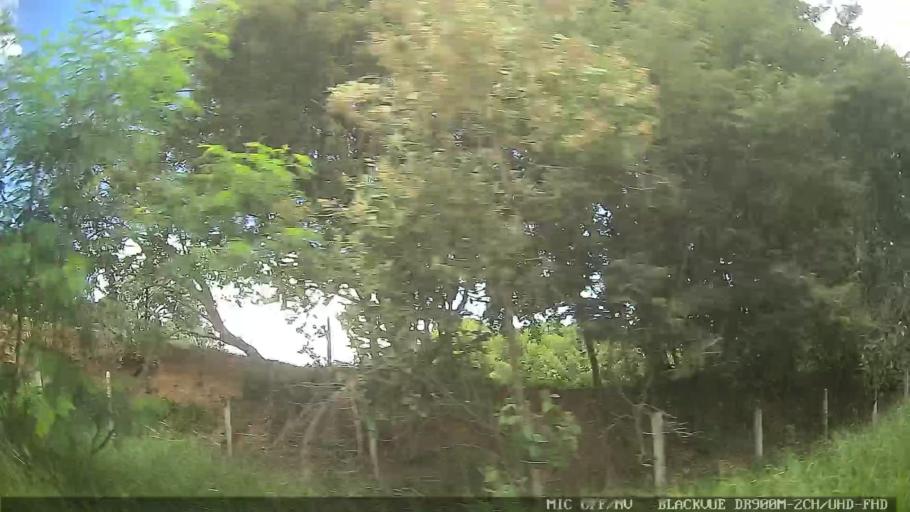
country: BR
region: Sao Paulo
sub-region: Conchas
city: Conchas
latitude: -22.9996
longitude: -47.9996
